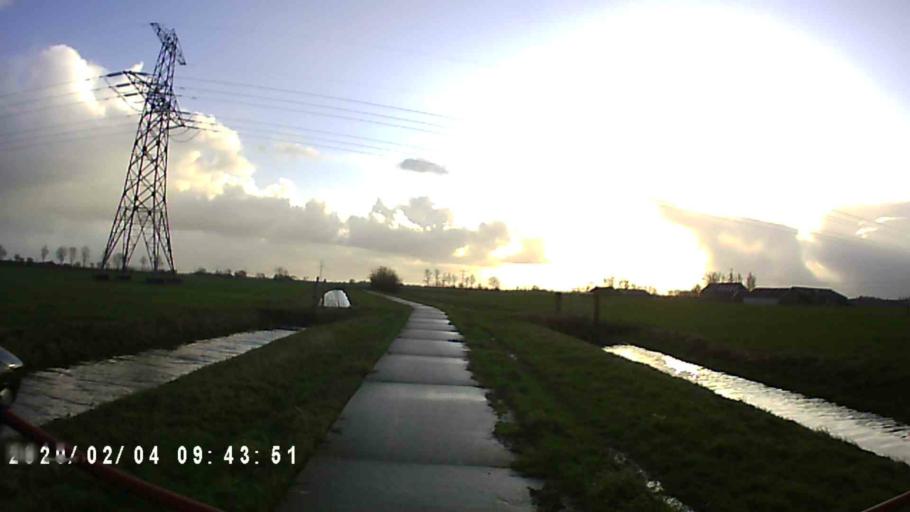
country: NL
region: Groningen
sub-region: Gemeente Zuidhorn
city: Aduard
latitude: 53.2937
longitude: 6.4788
